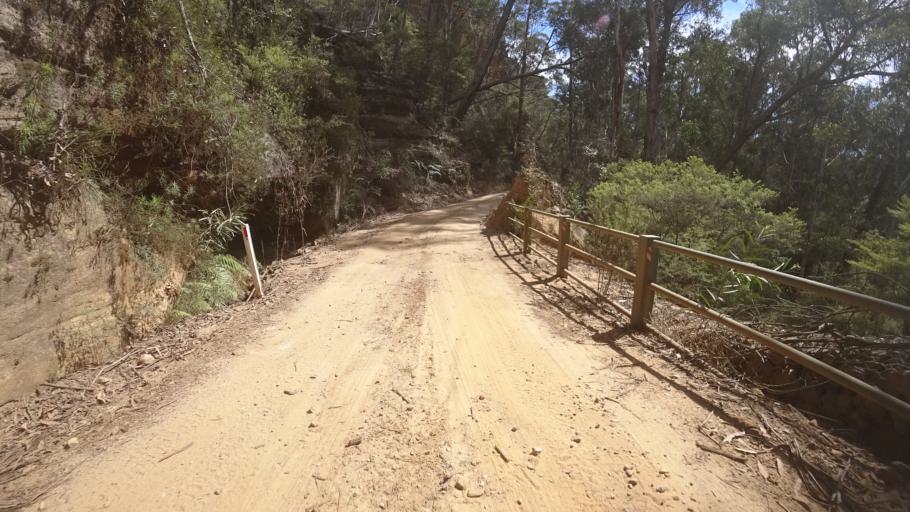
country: AU
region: New South Wales
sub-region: Lithgow
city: Lithgow
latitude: -33.2493
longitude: 150.2221
